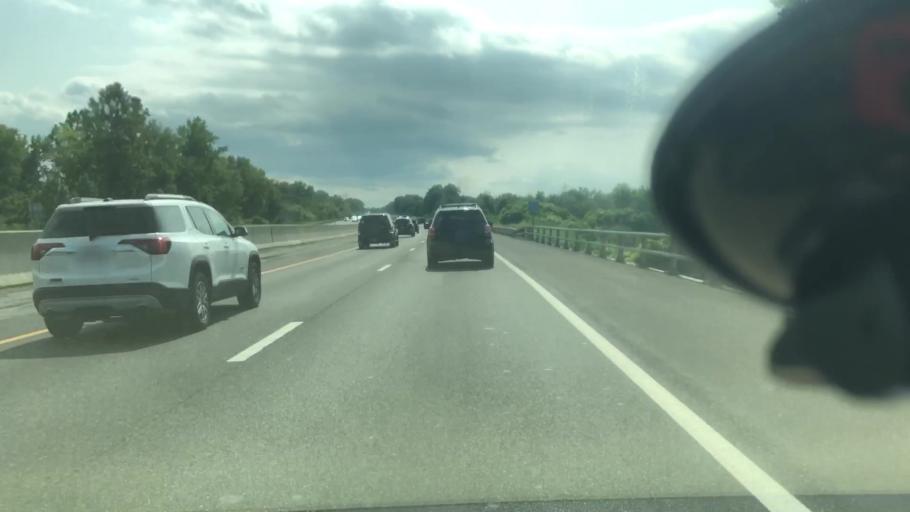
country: US
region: New York
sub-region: Ulster County
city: Hurley
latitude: 41.9443
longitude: -74.0321
